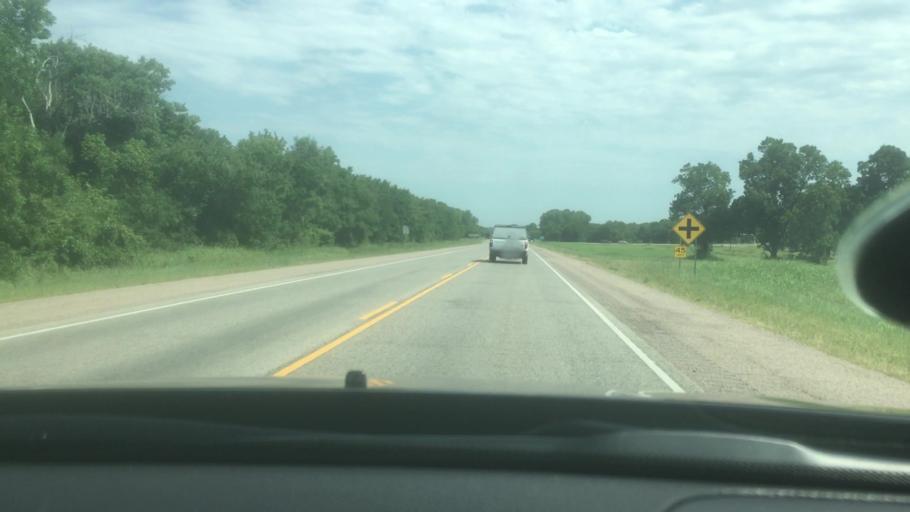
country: US
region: Oklahoma
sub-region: Seminole County
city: Maud
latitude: 35.0686
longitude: -96.9313
